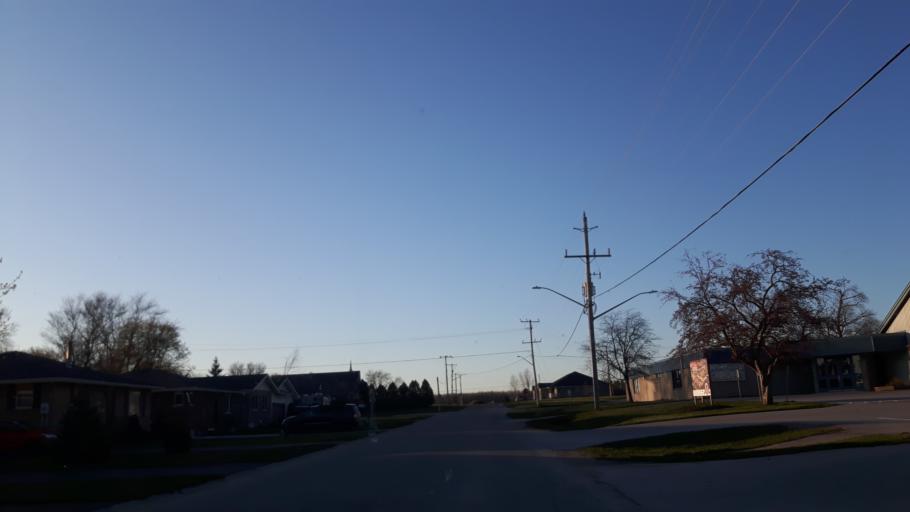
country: CA
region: Ontario
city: Bluewater
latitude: 43.5833
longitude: -81.5191
